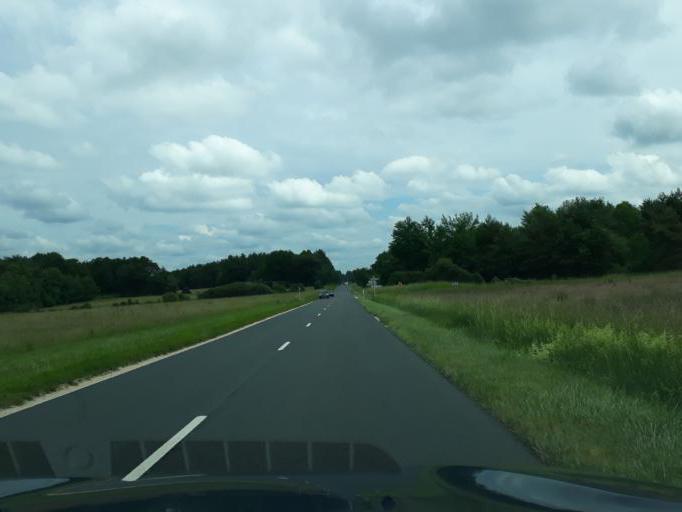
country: FR
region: Centre
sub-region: Departement du Loir-et-Cher
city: Lamotte-Beuvron
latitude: 47.5768
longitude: 1.9761
